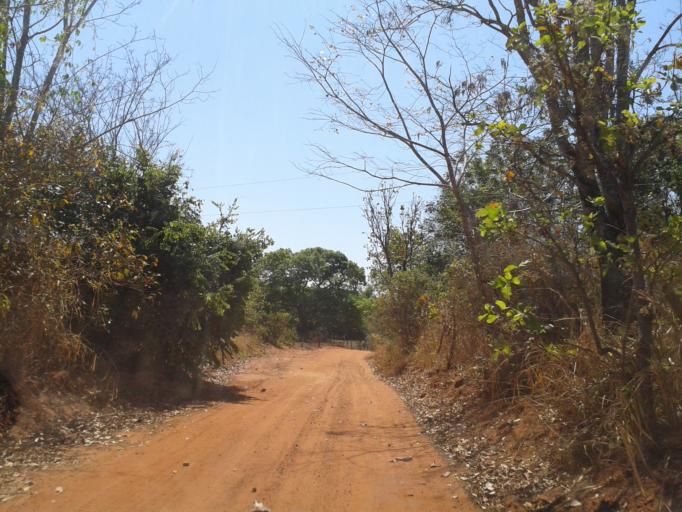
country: BR
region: Minas Gerais
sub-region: Ituiutaba
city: Ituiutaba
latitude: -19.0877
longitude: -49.2992
